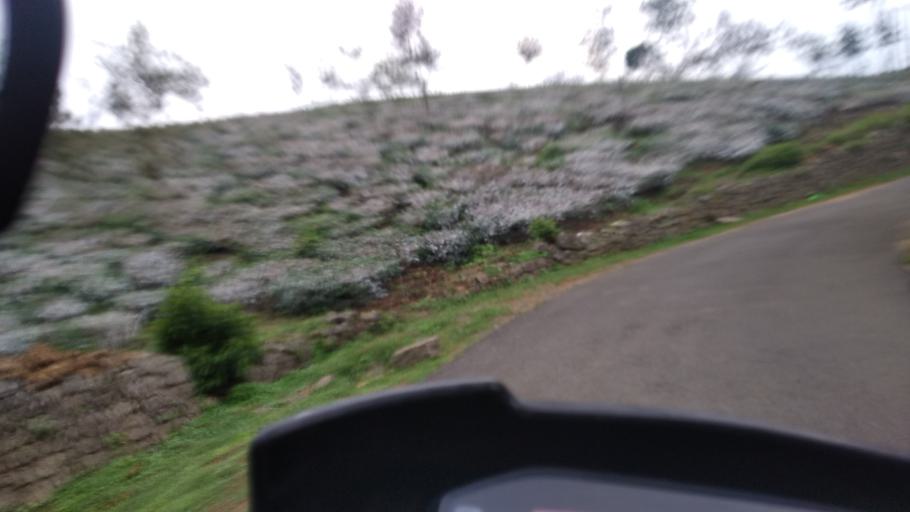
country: IN
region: Tamil Nadu
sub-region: Theni
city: Gudalur
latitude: 9.5414
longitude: 77.0450
